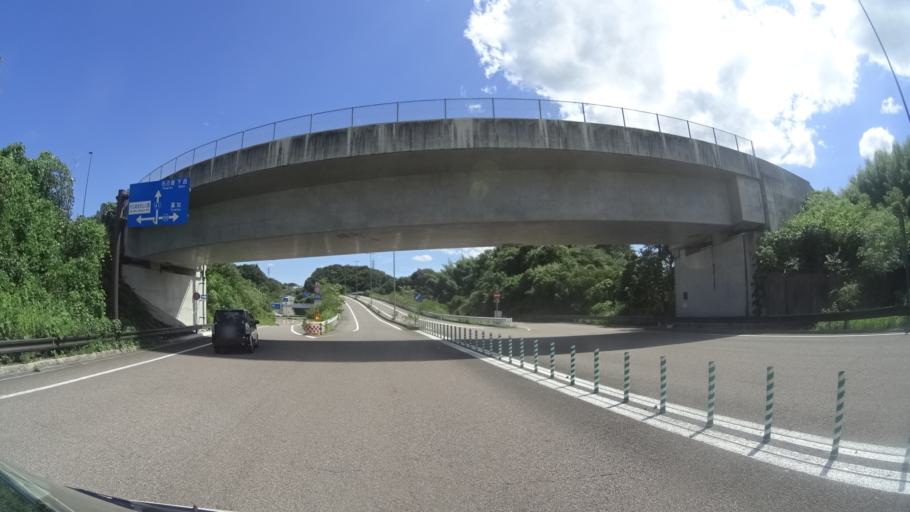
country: JP
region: Gifu
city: Minokamo
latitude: 35.4710
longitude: 137.0253
